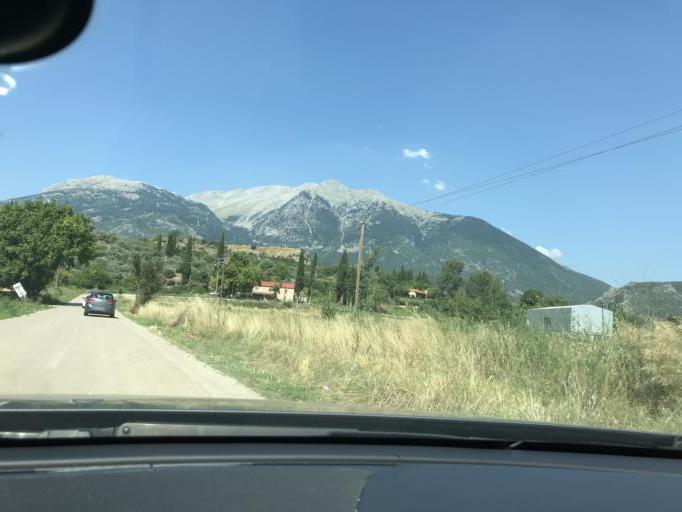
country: GR
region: Central Greece
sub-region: Nomos Fthiotidos
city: Kato Tithorea
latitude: 38.5172
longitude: 22.7513
